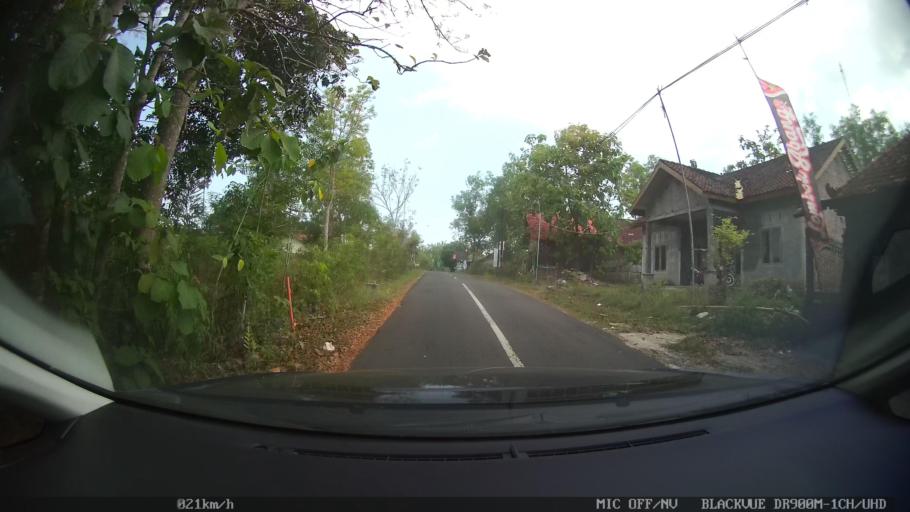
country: ID
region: Daerah Istimewa Yogyakarta
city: Bantul
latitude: -7.8610
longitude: 110.3079
